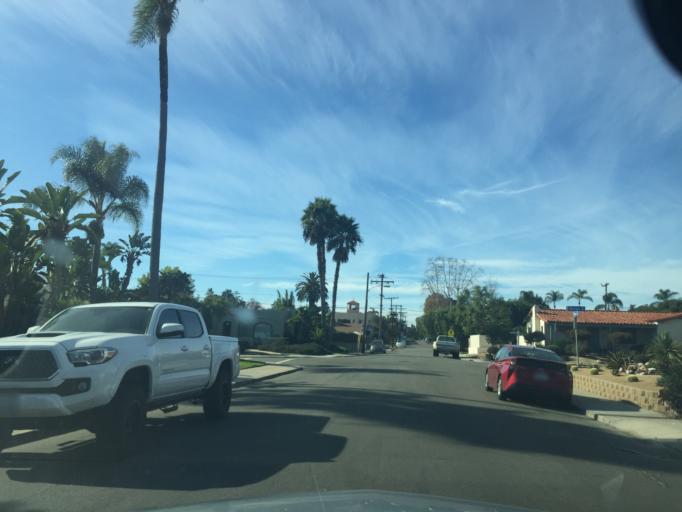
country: US
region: California
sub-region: San Diego County
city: San Diego
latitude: 32.7649
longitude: -117.1037
